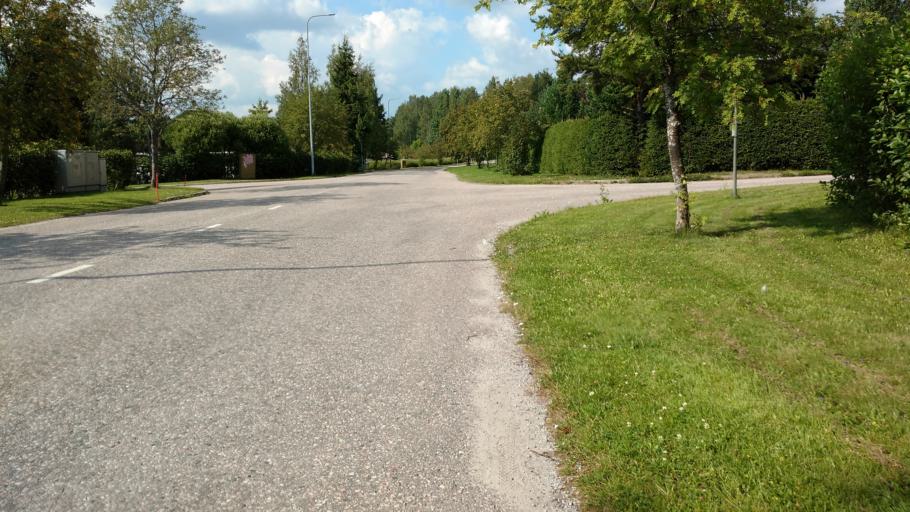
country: FI
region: Varsinais-Suomi
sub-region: Salo
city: Salo
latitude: 60.3899
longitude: 23.1694
